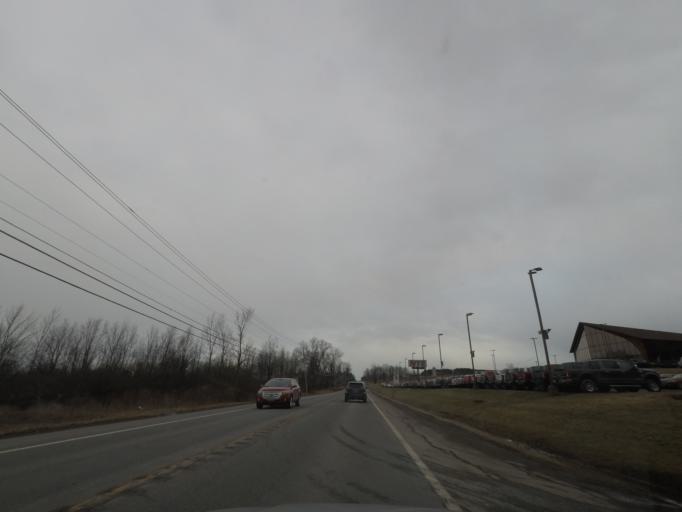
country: US
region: New York
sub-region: Madison County
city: Wampsville
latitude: 43.0765
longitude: -75.6854
